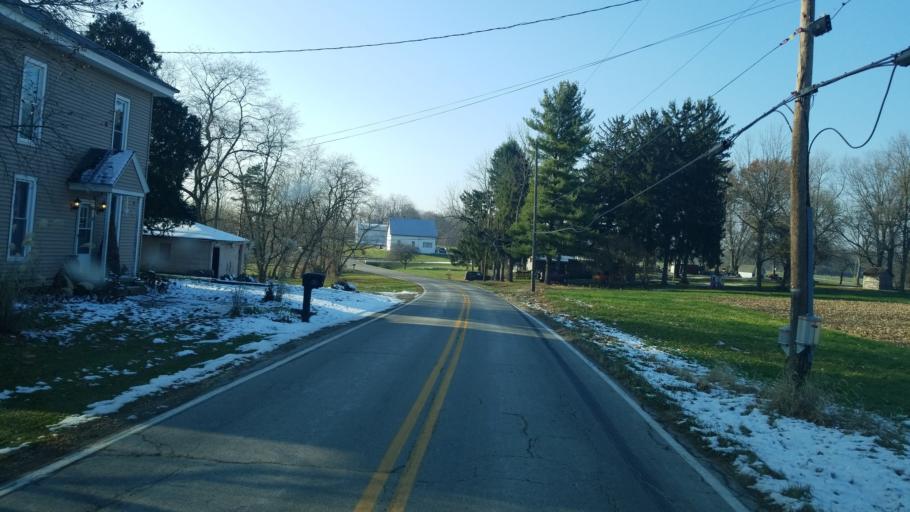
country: US
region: Ohio
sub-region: Richland County
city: Lexington
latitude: 40.6189
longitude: -82.5879
